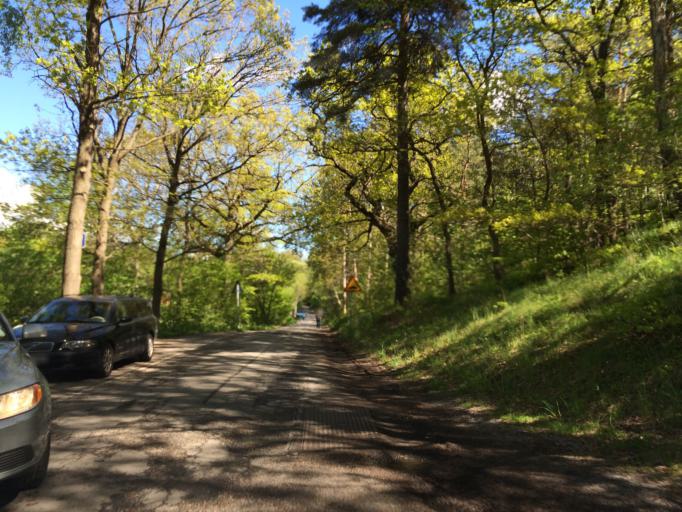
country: SE
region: Stockholm
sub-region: Solna Kommun
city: Solna
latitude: 59.3109
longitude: 17.9956
